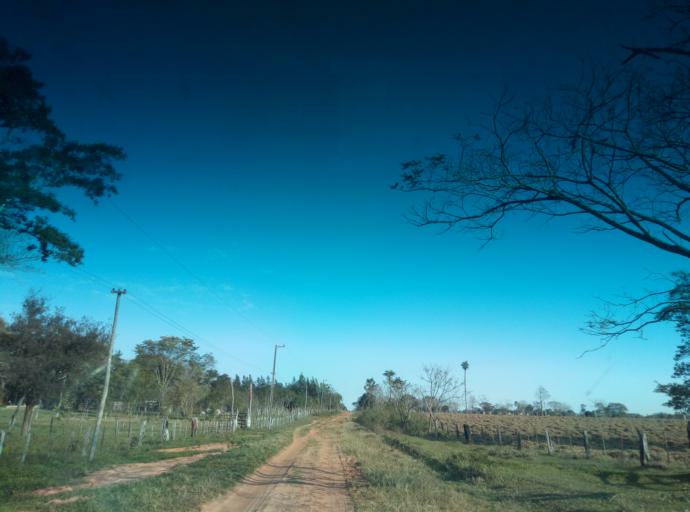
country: PY
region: Caaguazu
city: Doctor Cecilio Baez
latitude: -25.1671
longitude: -56.2320
